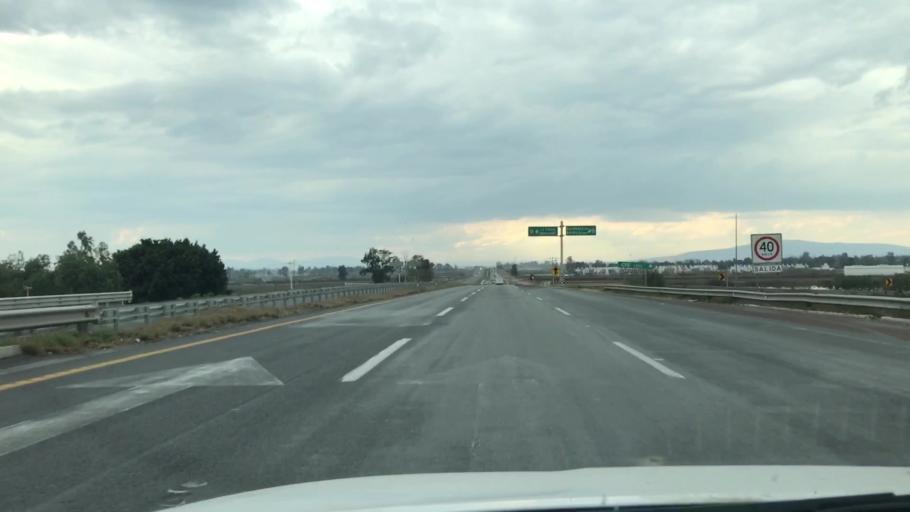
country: MX
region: Guanajuato
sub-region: Irapuato
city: Cuarta Brigada
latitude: 20.6542
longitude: -101.2994
